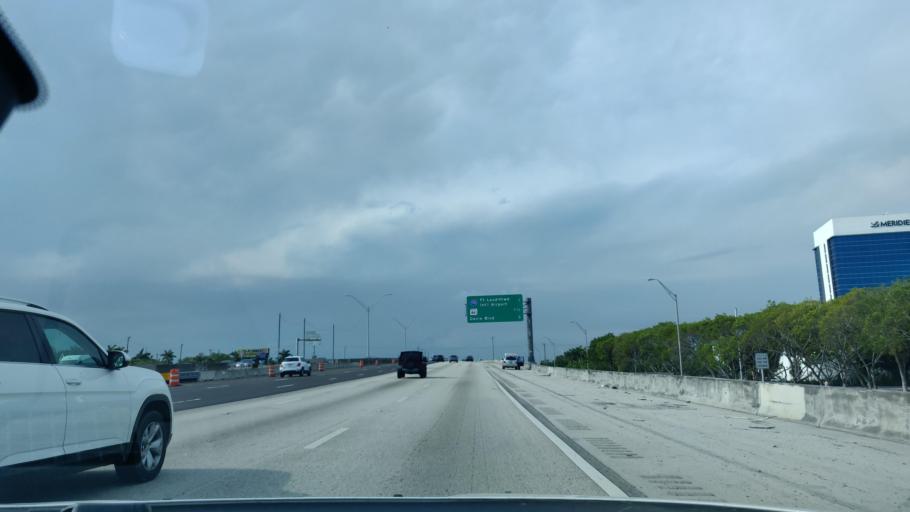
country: US
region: Florida
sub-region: Broward County
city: Dania Beach
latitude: 26.0549
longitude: -80.1687
